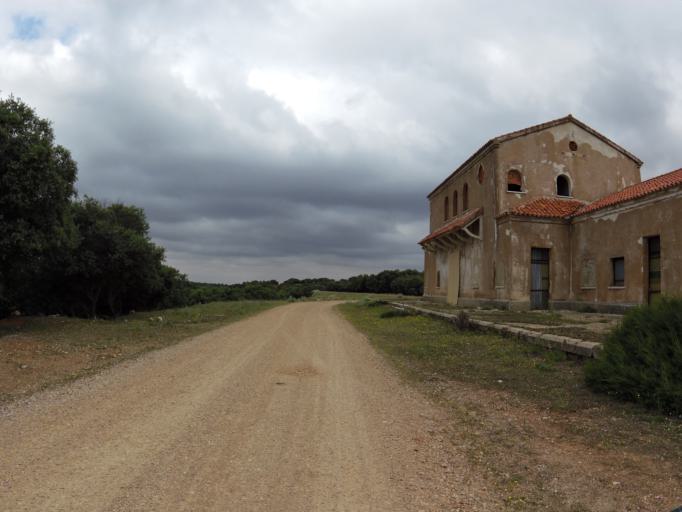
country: ES
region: Castille-La Mancha
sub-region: Provincia de Albacete
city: Robledo
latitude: 38.7437
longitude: -2.4693
